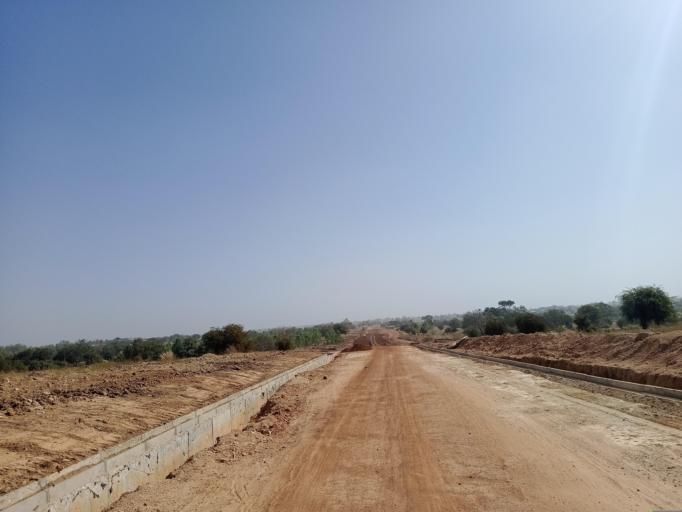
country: BF
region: Centre-Est
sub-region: Province du Boulgou
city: Garango
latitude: 11.5015
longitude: -0.5056
